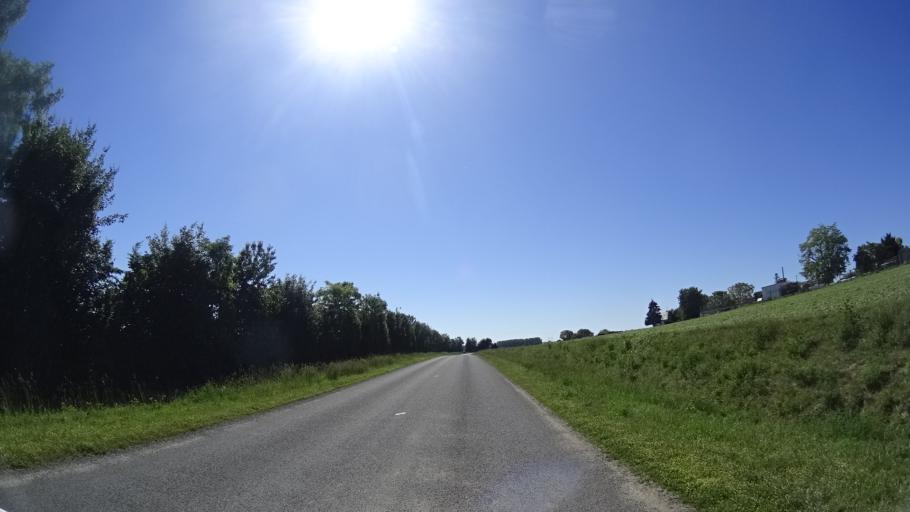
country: FR
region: Pays de la Loire
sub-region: Departement de Maine-et-Loire
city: Doue-la-Fontaine
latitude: 47.2355
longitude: -0.2941
